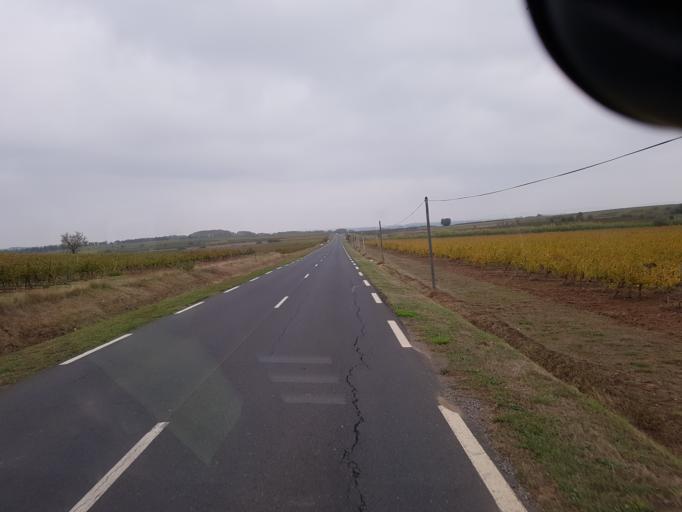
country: FR
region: Languedoc-Roussillon
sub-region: Departement de l'Herault
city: Pinet
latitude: 43.3934
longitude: 3.5382
